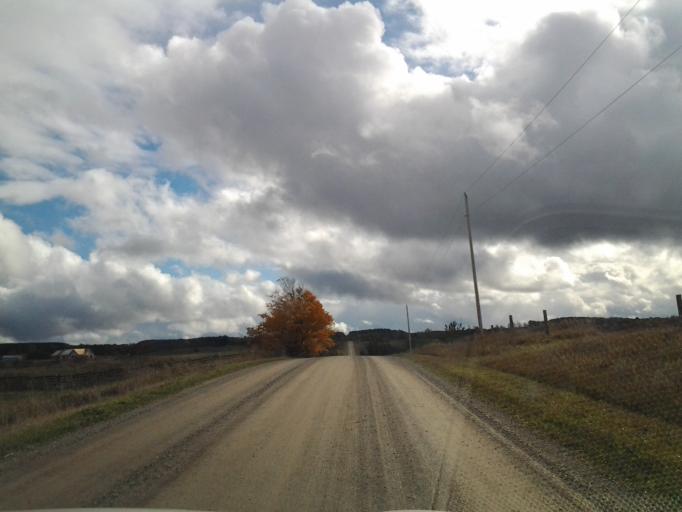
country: CA
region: Ontario
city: Shelburne
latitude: 44.0855
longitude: -80.1042
